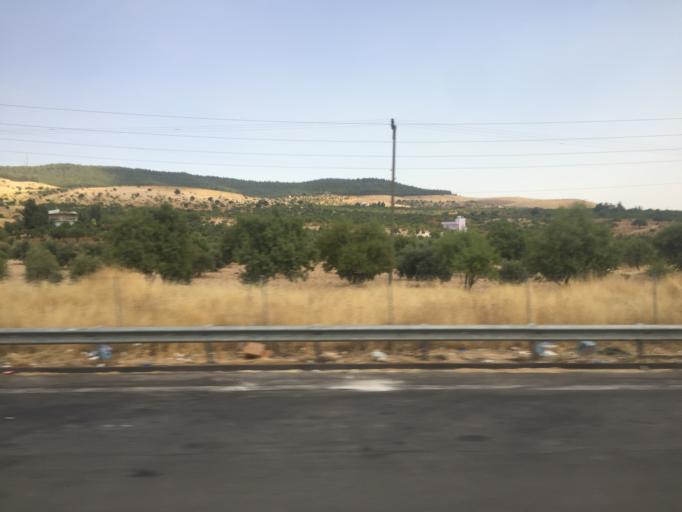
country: TR
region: Sanliurfa
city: Akziyaret
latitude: 37.2647
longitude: 38.7983
